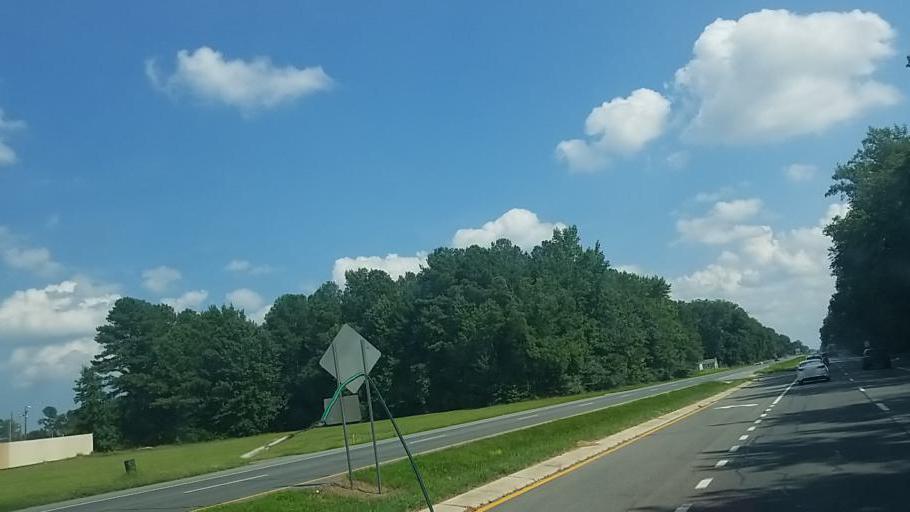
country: US
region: Delaware
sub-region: Sussex County
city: Georgetown
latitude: 38.6504
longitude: -75.3657
